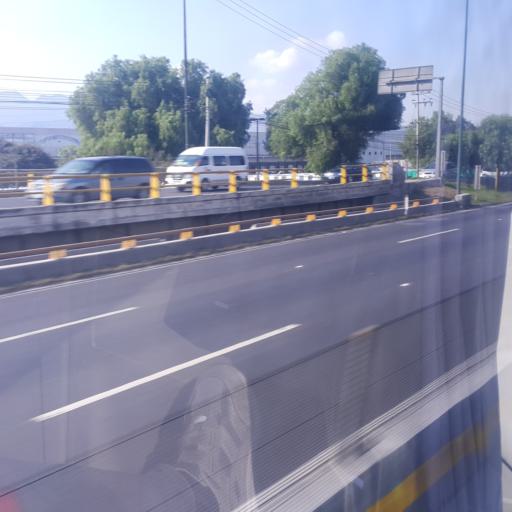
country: MX
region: Mexico
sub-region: Cuautitlan
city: San Jose del Puente
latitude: 19.7037
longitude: -99.2055
